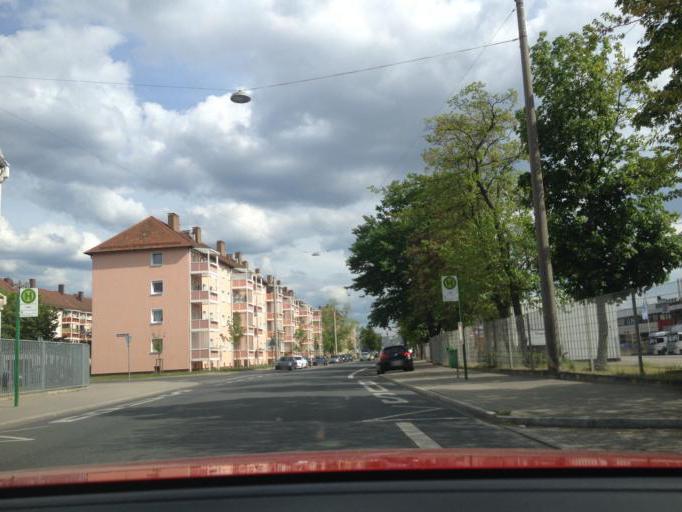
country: DE
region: Bavaria
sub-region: Regierungsbezirk Mittelfranken
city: Furth
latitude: 49.4620
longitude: 11.0071
